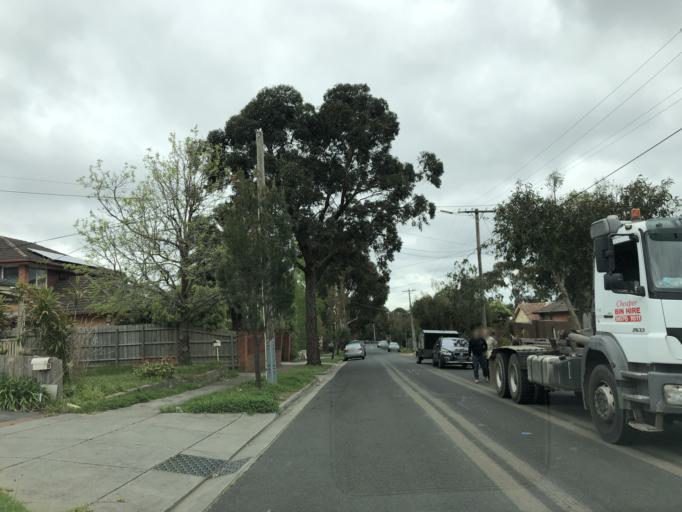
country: AU
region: Victoria
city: Burwood East
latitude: -37.8537
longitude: 145.1458
